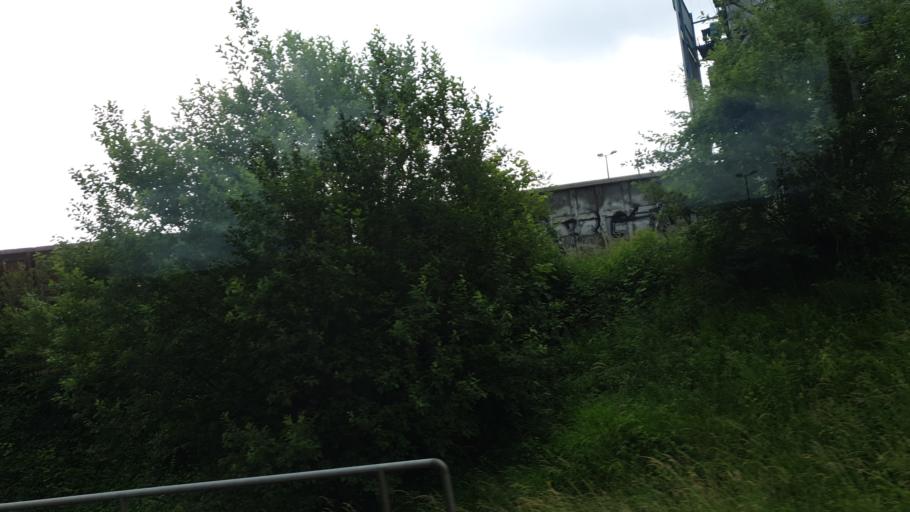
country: CH
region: Saint Gallen
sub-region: Wahlkreis Rorschach
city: Goldach
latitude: 47.4724
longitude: 9.4468
